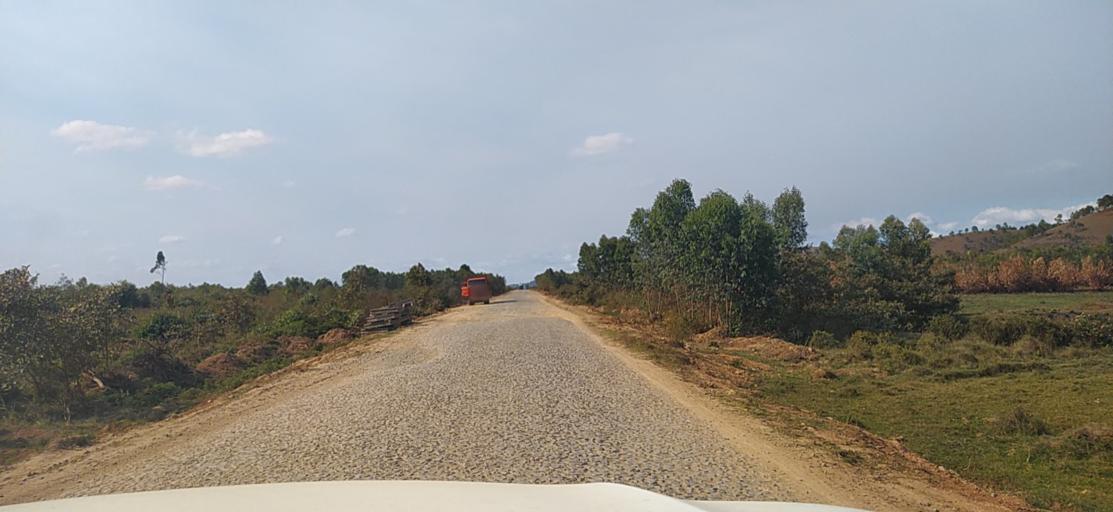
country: MG
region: Alaotra Mangoro
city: Moramanga
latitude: -18.6838
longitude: 48.2717
